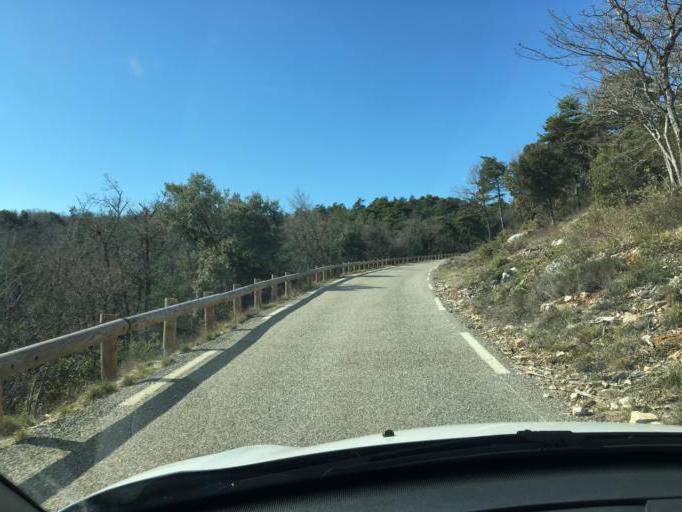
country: FR
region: Provence-Alpes-Cote d'Azur
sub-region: Departement du Vaucluse
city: Saint-Saturnin-les-Apt
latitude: 43.9648
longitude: 5.4608
